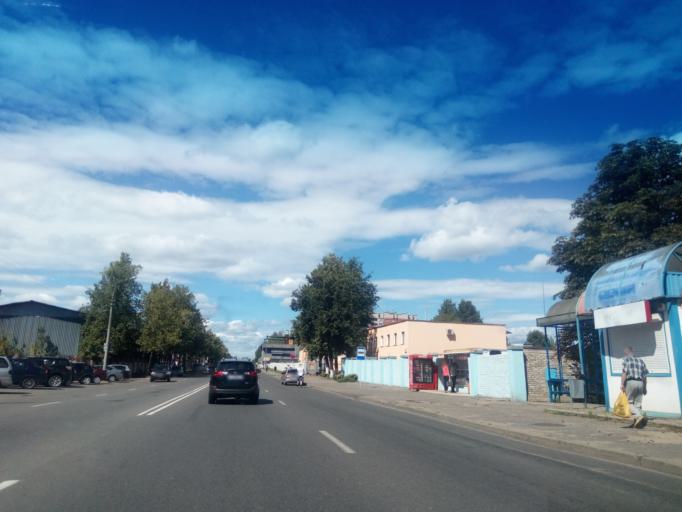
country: BY
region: Vitebsk
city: Polatsk
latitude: 55.4912
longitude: 28.7792
